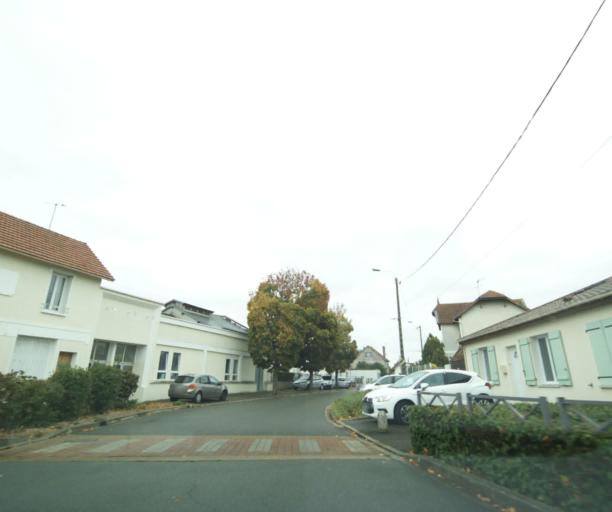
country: FR
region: Centre
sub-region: Departement d'Eure-et-Loir
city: Dreux
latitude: 48.7294
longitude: 1.3748
